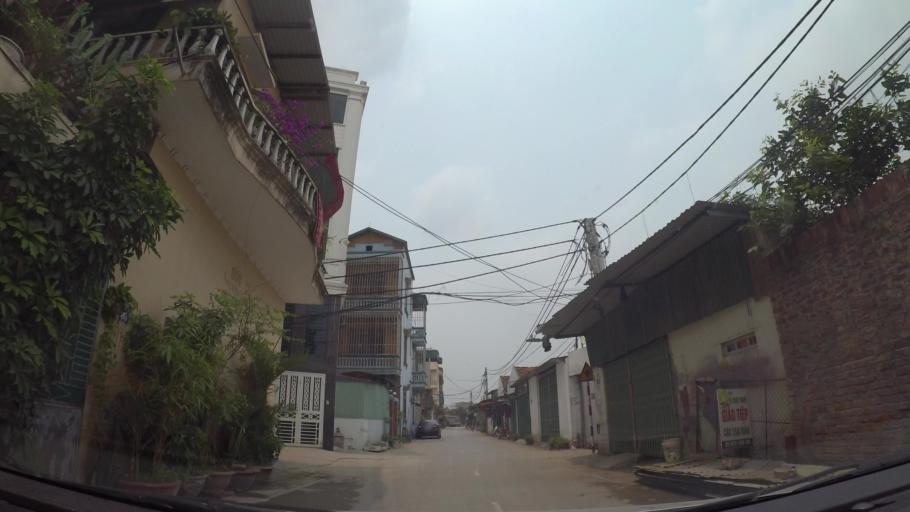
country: VN
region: Ha Noi
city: Ha Dong
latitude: 20.9913
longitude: 105.7414
